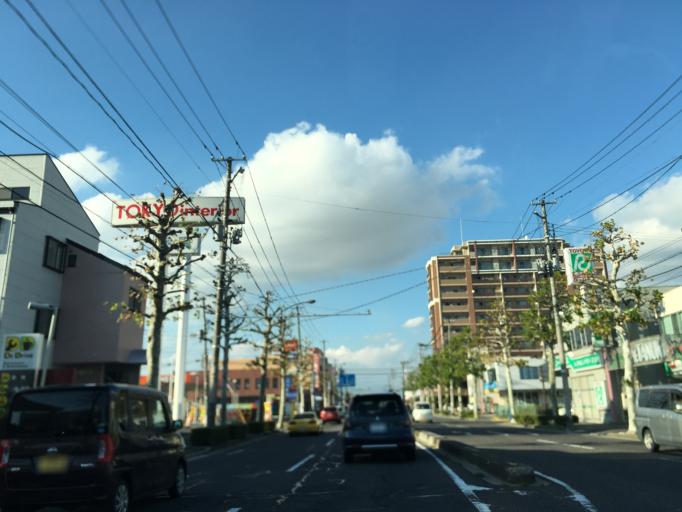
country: JP
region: Fukushima
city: Koriyama
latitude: 37.4063
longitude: 140.3620
